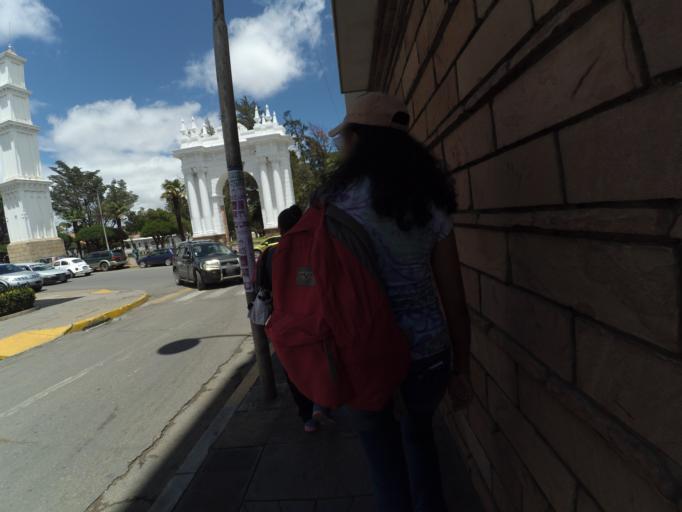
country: BO
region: Chuquisaca
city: Sucre
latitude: -19.0431
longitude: -65.2627
